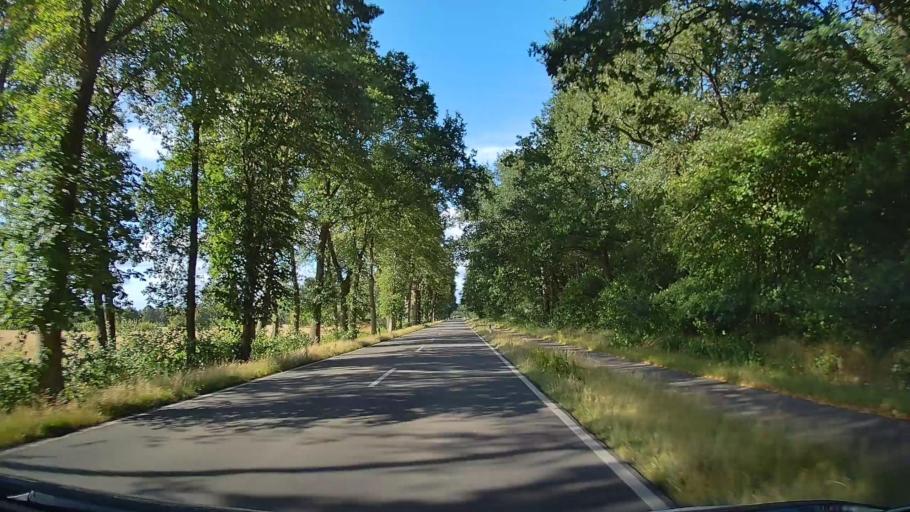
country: DE
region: Lower Saxony
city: Bosel
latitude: 52.9450
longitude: 7.8965
